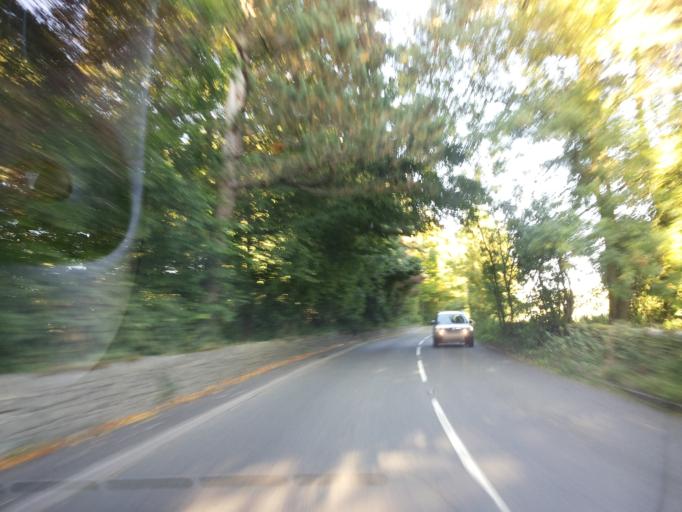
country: GB
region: England
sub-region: Derbyshire
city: Bakewell
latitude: 53.2317
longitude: -1.7016
